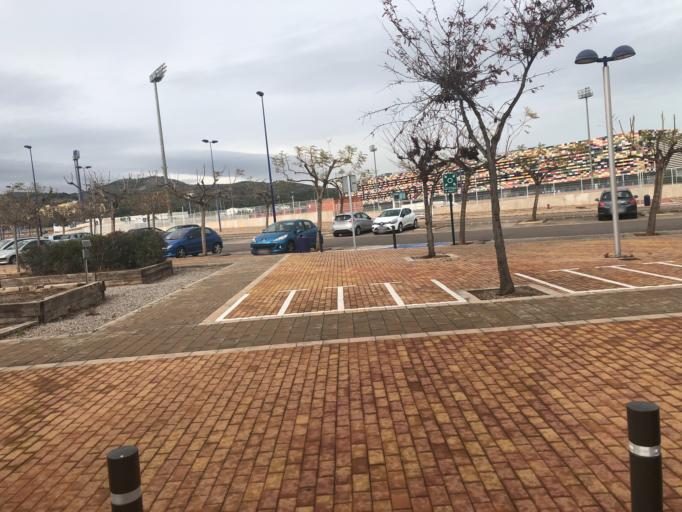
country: ES
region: Valencia
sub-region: Provincia de Castello
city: Castello de la Plana
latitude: 39.9941
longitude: -0.0738
